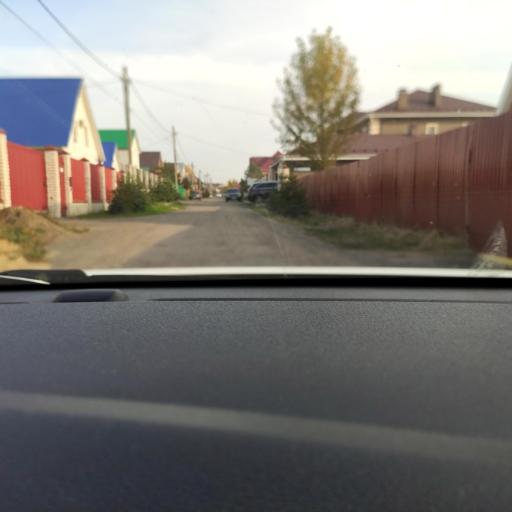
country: RU
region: Tatarstan
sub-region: Gorod Kazan'
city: Kazan
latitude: 55.8231
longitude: 49.2246
